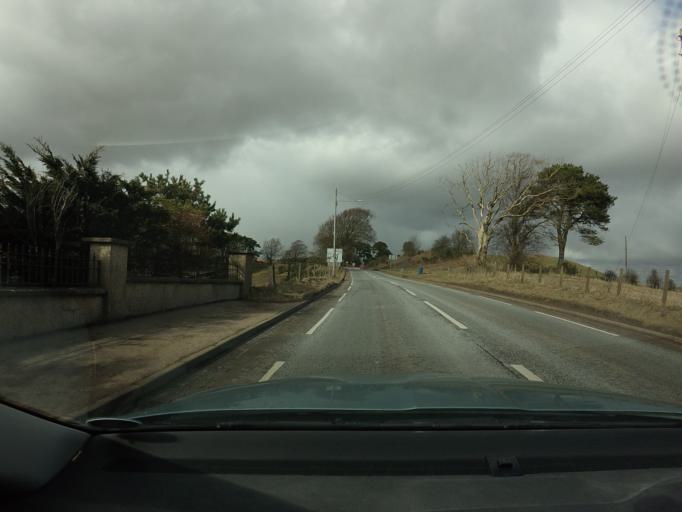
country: GB
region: Scotland
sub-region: South Lanarkshire
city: Lanark
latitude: 55.6572
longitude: -3.7275
